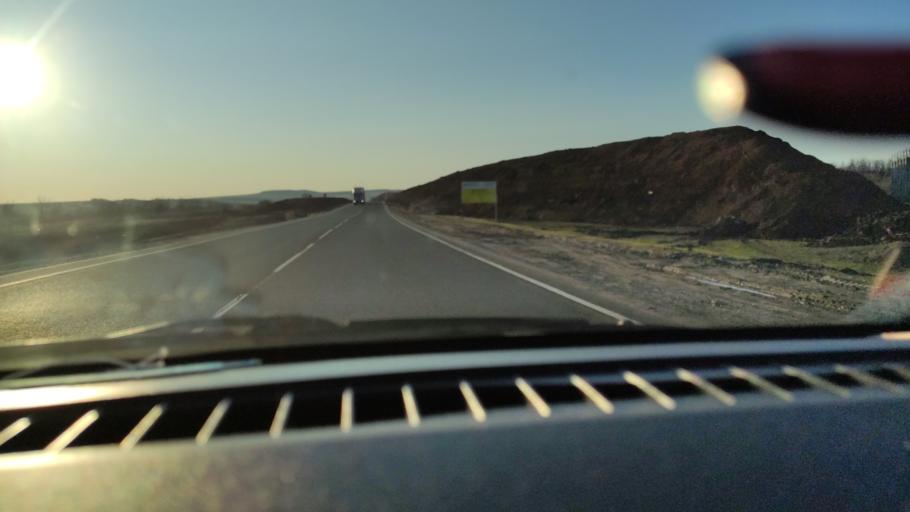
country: RU
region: Saratov
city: Sennoy
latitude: 52.1606
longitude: 47.0543
